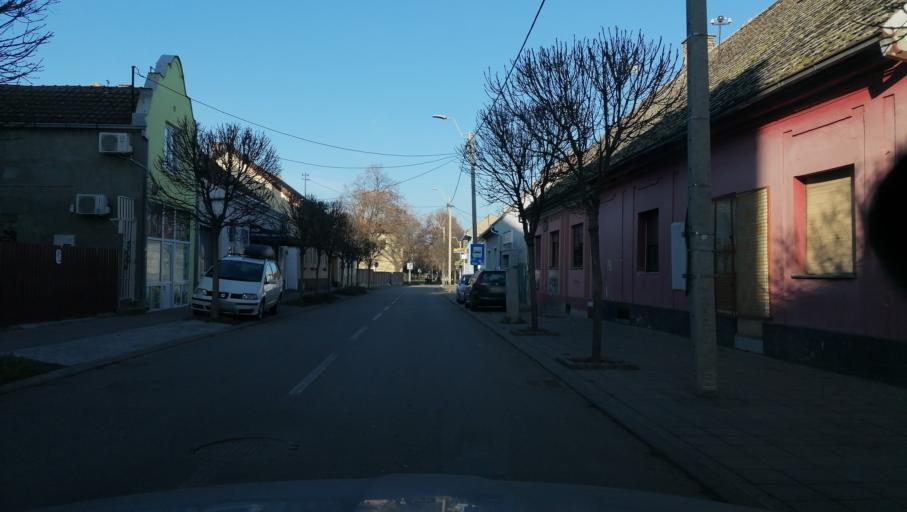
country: RS
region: Autonomna Pokrajina Vojvodina
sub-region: Sremski Okrug
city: Sremska Mitrovica
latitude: 44.9687
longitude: 19.6127
